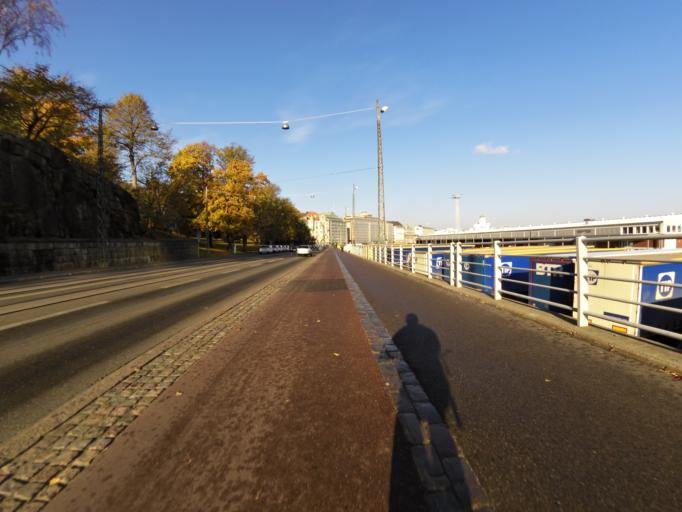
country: FI
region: Uusimaa
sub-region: Helsinki
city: Helsinki
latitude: 60.1623
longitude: 24.9558
